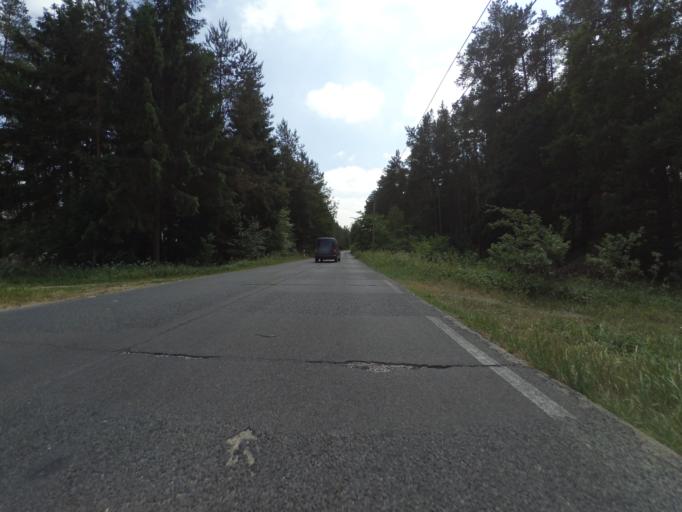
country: DE
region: Mecklenburg-Vorpommern
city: Plau am See
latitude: 53.4152
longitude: 12.3263
